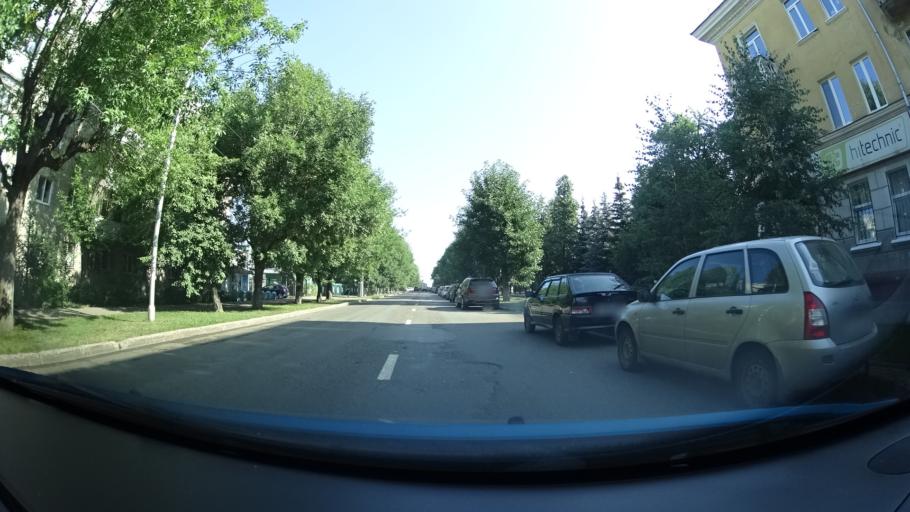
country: RU
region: Bashkortostan
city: Ufa
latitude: 54.7318
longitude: 55.9631
